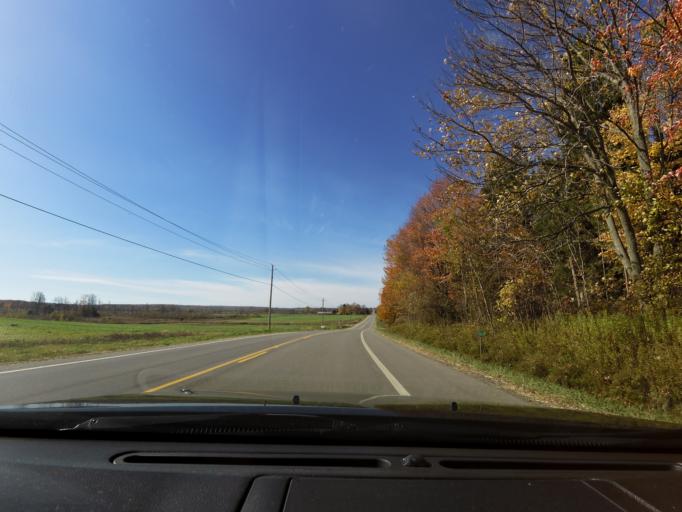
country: US
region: New York
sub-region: Wyoming County
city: Warsaw
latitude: 42.6524
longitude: -78.1397
